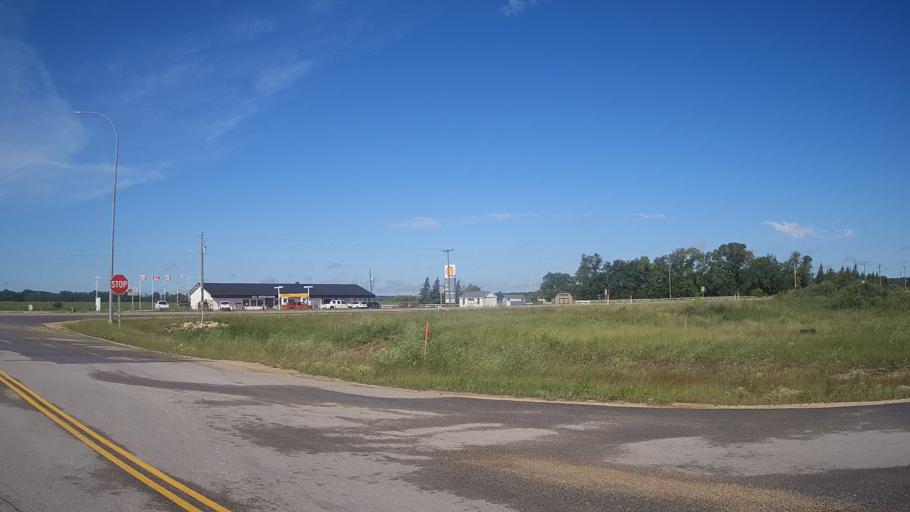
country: CA
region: Manitoba
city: Stonewall
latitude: 50.2095
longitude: -97.6656
